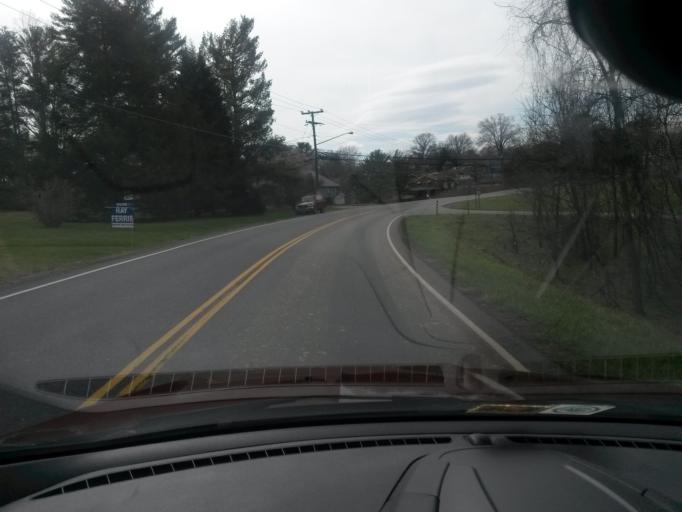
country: US
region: Virginia
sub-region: Roanoke County
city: Cave Spring
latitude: 37.2432
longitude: -80.0069
